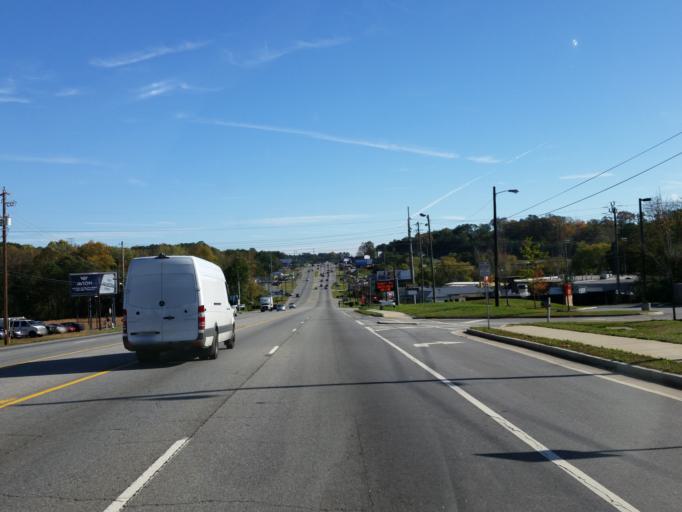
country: US
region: Georgia
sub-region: Cobb County
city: Marietta
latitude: 33.9657
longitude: -84.5341
